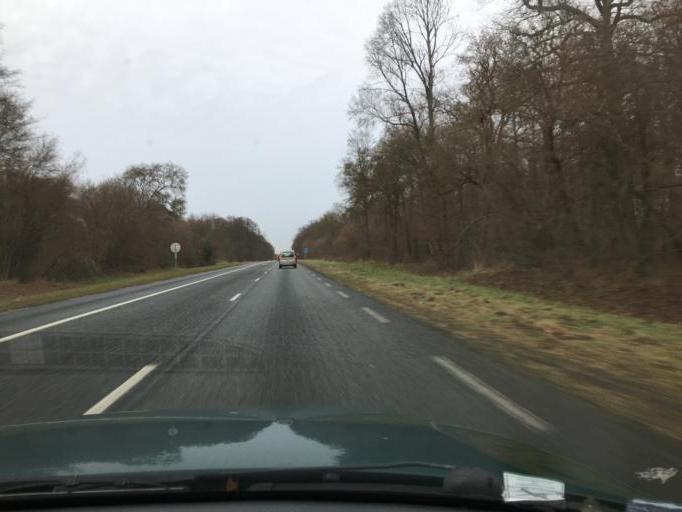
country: FR
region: Picardie
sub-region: Departement de l'Oise
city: Thiers-sur-Theve
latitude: 49.1691
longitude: 2.5589
